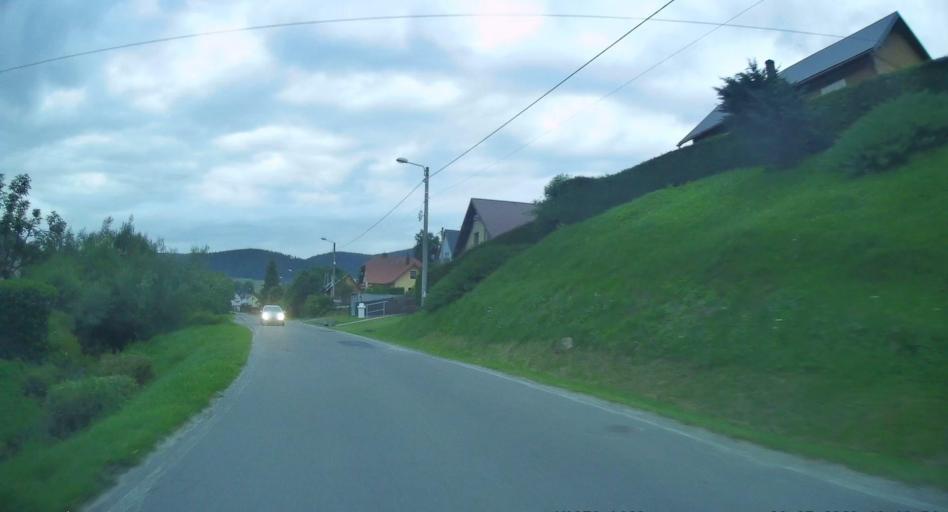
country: PL
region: Lesser Poland Voivodeship
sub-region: Powiat nowosadecki
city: Muszyna
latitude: 49.3820
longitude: 20.9219
